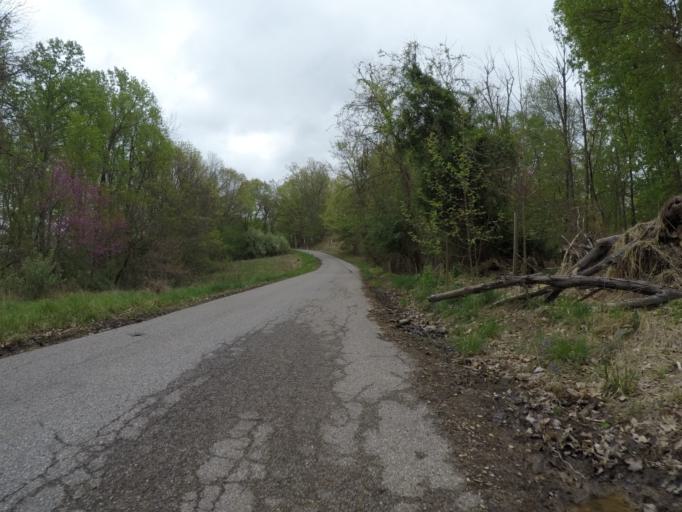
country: US
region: West Virginia
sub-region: Cabell County
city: Barboursville
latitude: 38.3980
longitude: -82.2587
